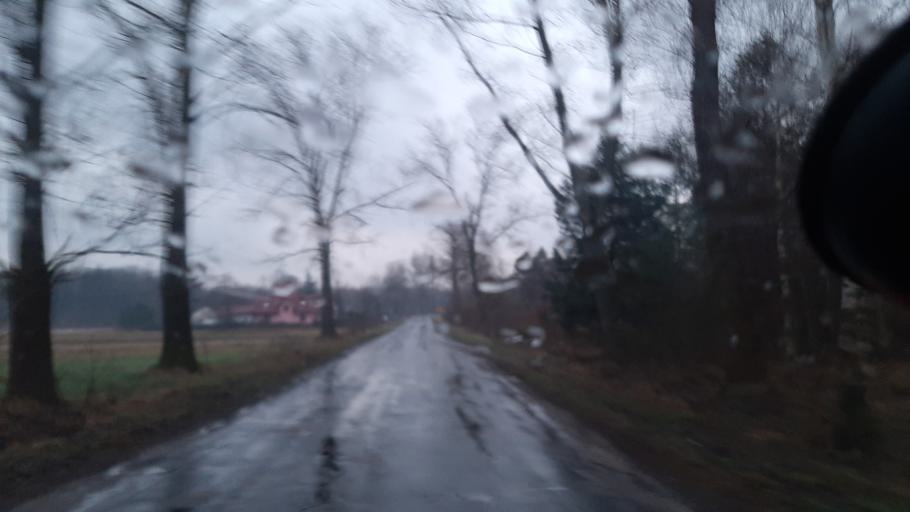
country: PL
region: Lublin Voivodeship
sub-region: Powiat lubartowski
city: Firlej
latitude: 51.5313
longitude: 22.5025
